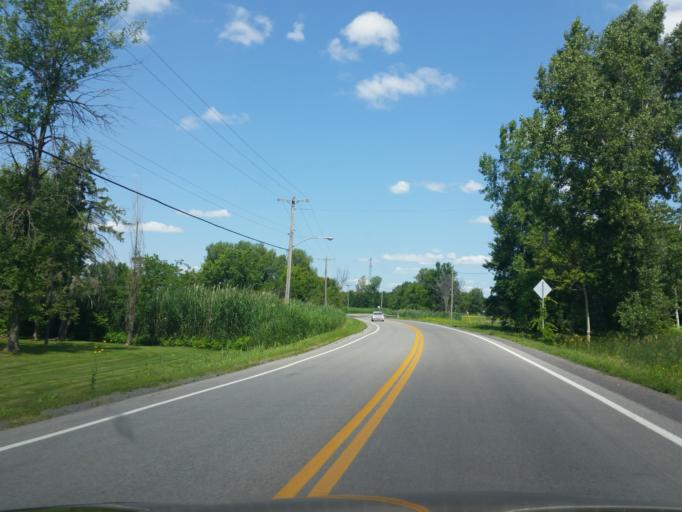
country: CA
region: Quebec
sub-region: Monteregie
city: Richelieu
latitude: 45.3852
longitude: -73.2580
